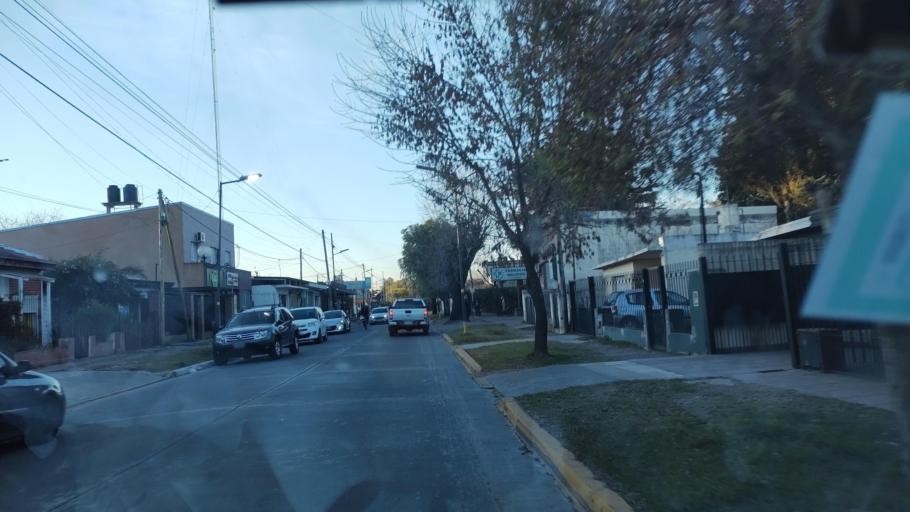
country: AR
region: Buenos Aires
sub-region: Partido de La Plata
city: La Plata
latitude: -34.9018
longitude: -58.0436
